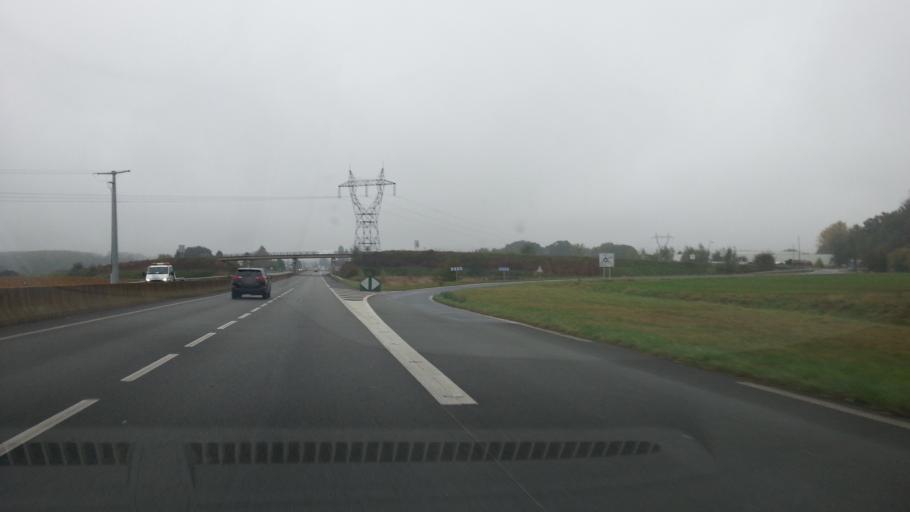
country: FR
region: Picardie
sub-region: Departement de l'Oise
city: Breuil-le-Vert
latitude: 49.3523
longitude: 2.4273
